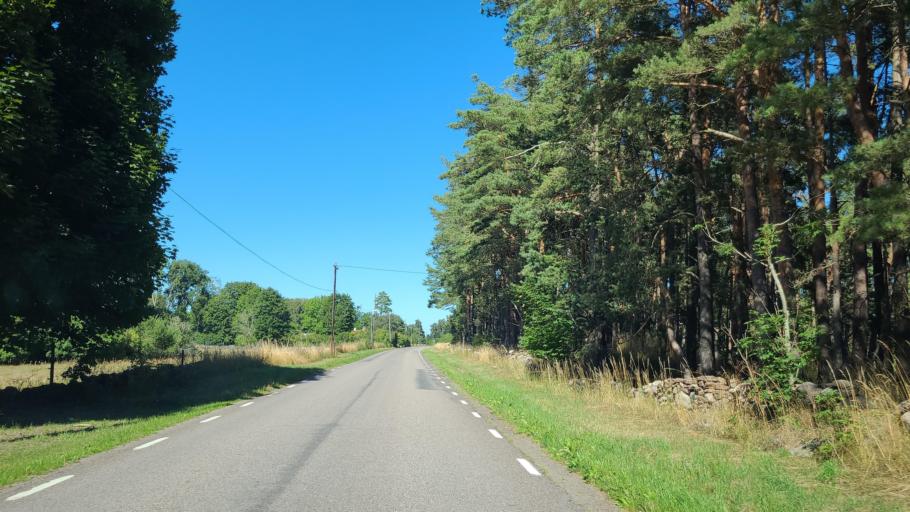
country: SE
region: Kalmar
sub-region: Borgholms Kommun
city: Borgholm
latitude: 56.8336
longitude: 16.7752
